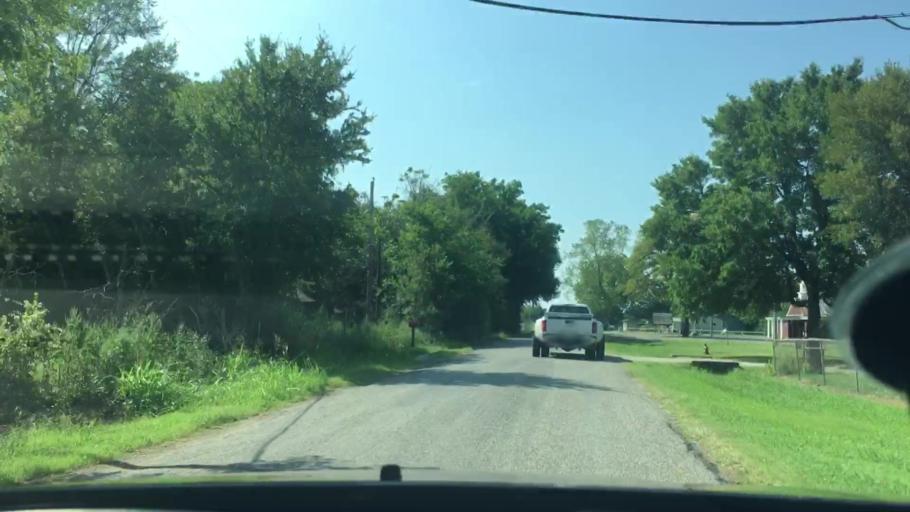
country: US
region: Oklahoma
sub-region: Bryan County
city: Colbert
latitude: 33.9093
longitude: -96.5378
